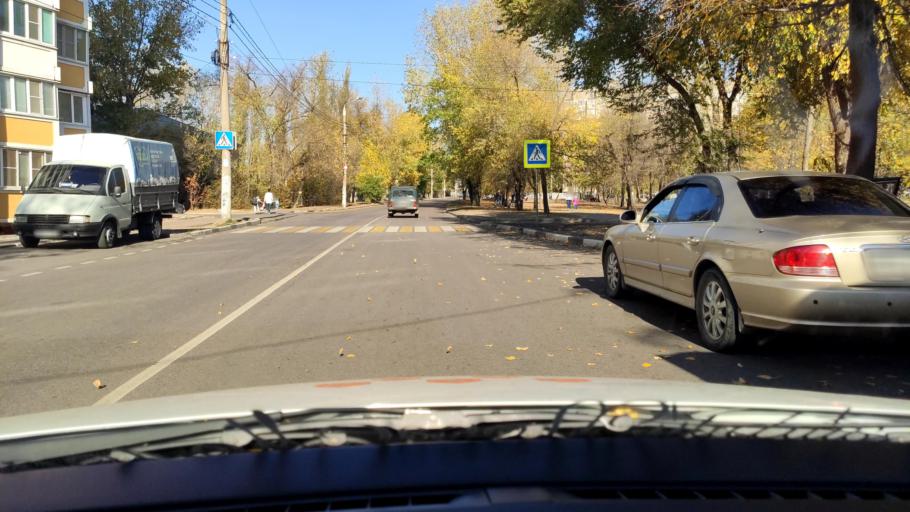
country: RU
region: Voronezj
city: Pridonskoy
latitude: 51.6834
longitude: 39.0769
